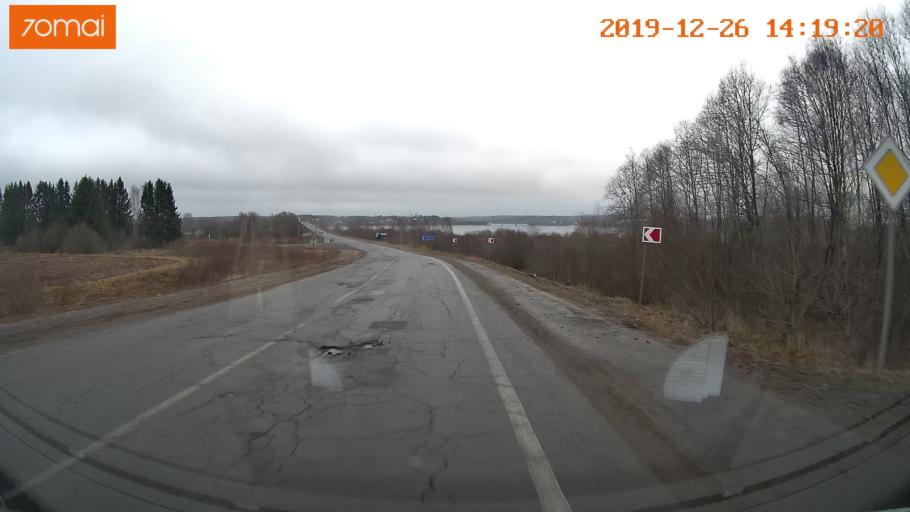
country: RU
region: Jaroslavl
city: Poshekhon'ye
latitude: 58.5107
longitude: 39.1123
